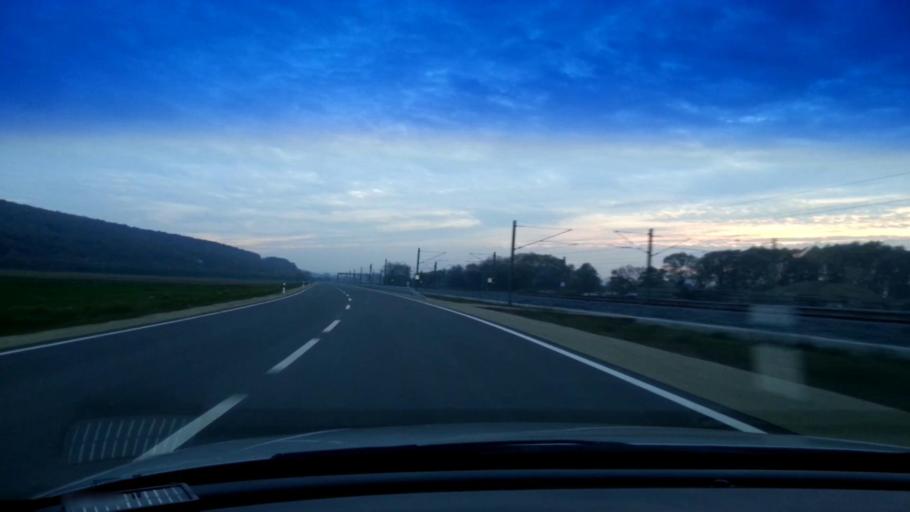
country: DE
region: Bavaria
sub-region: Upper Franconia
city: Zapfendorf
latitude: 50.0076
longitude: 10.9202
